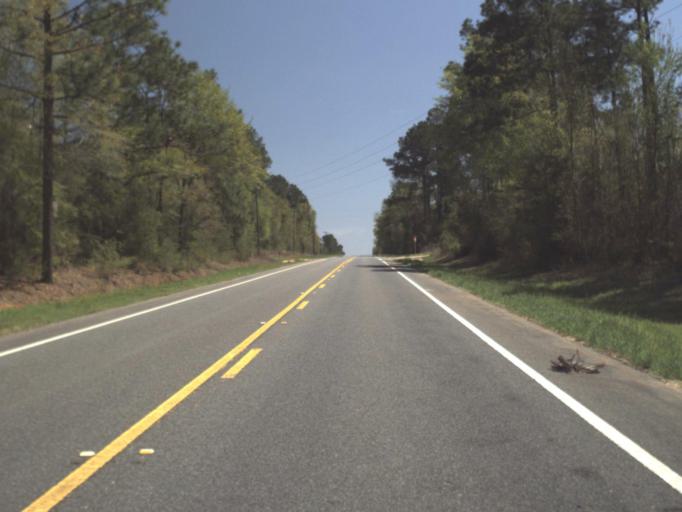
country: US
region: Alabama
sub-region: Geneva County
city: Geneva
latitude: 30.9607
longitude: -85.9940
